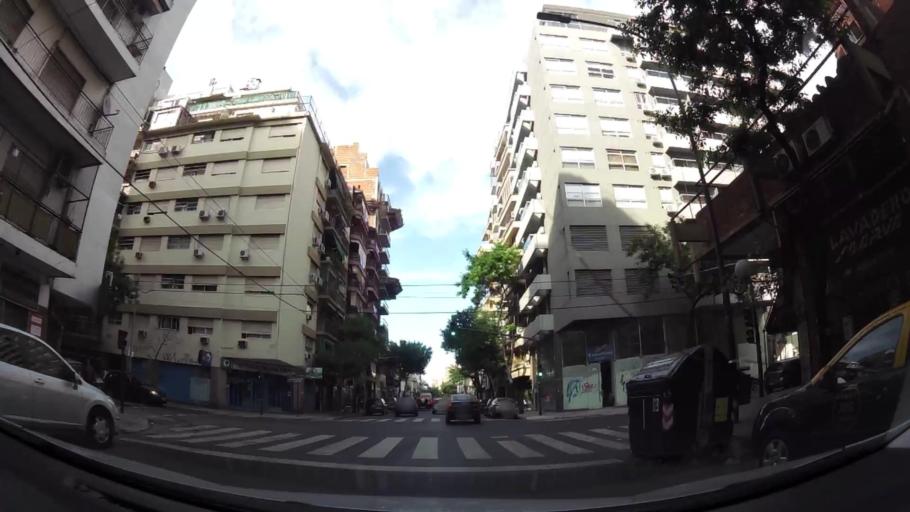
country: AR
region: Buenos Aires F.D.
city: Colegiales
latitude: -34.5605
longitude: -58.4635
